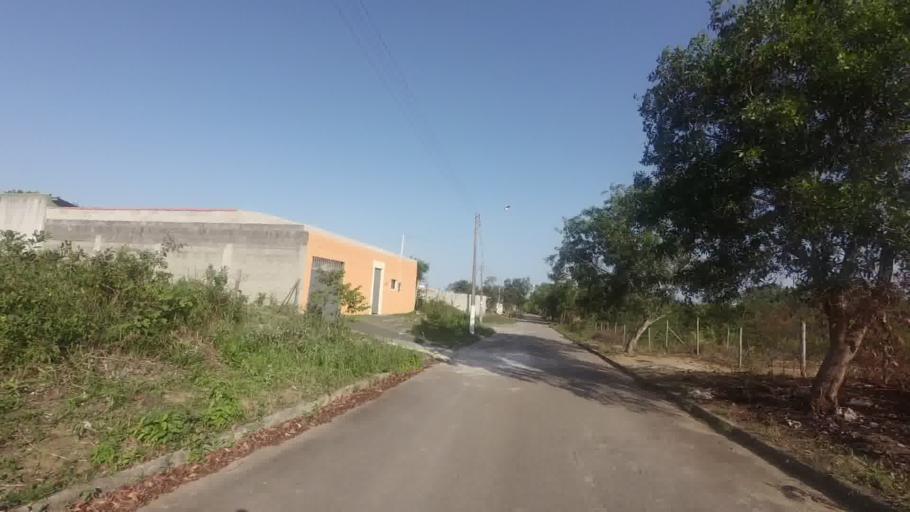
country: BR
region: Espirito Santo
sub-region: Guarapari
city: Guarapari
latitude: -20.7258
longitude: -40.5391
